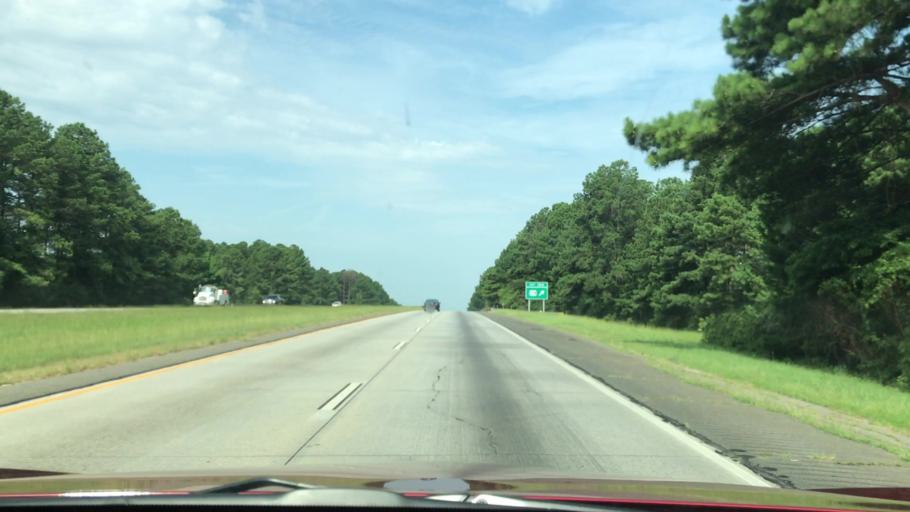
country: US
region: Georgia
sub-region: Taliaferro County
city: Crawfordville
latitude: 33.4994
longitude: -82.8018
